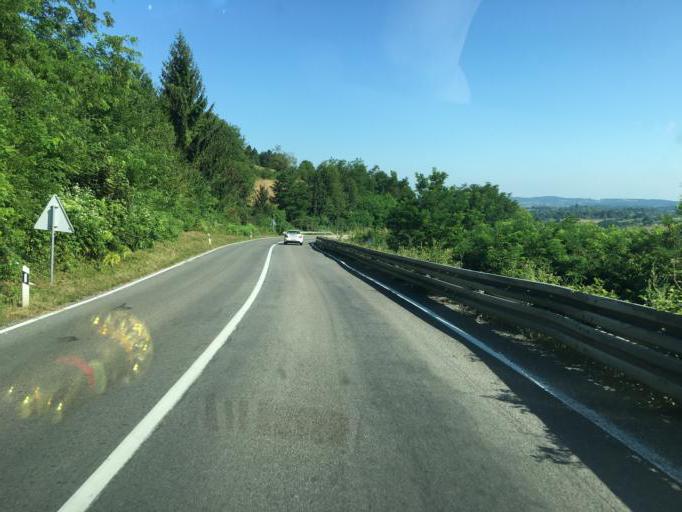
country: HR
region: Karlovacka
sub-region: Grad Karlovac
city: Slunj
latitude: 45.0865
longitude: 15.5947
